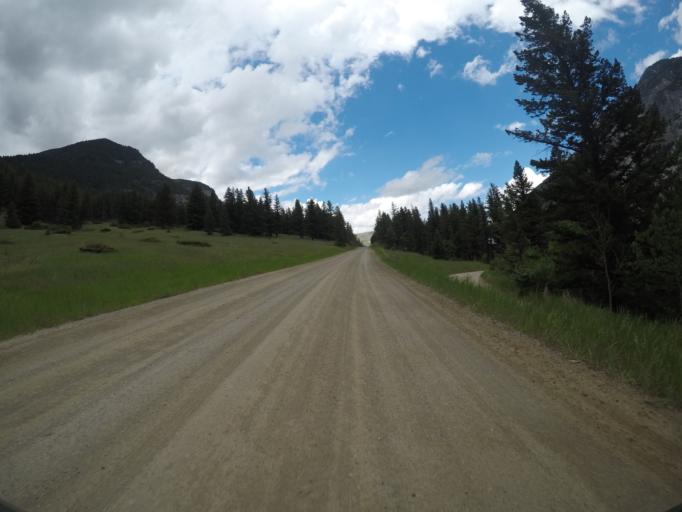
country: US
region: Montana
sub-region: Park County
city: Livingston
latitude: 45.4929
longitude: -110.2256
